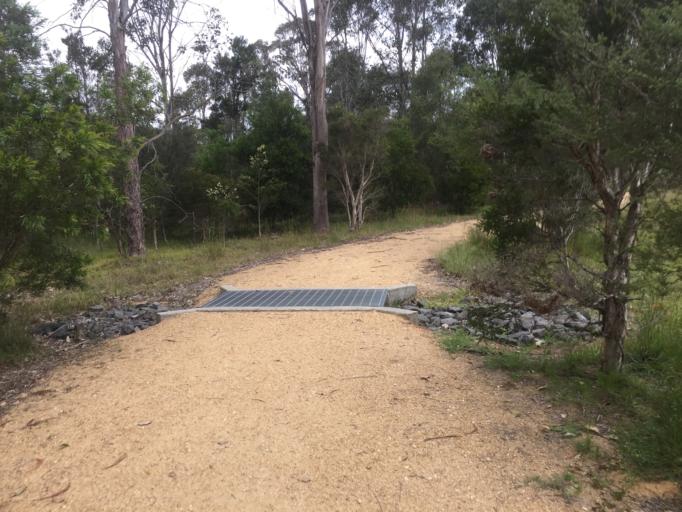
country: AU
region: New South Wales
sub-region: Blacktown
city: Doonside
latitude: -33.7860
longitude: 150.8694
